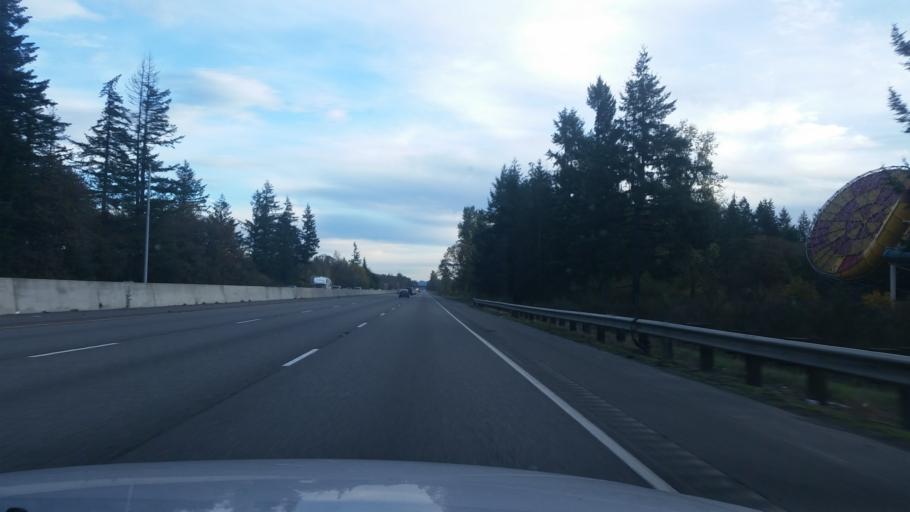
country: US
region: Washington
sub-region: Thurston County
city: Grand Mound
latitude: 46.7913
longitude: -123.0089
